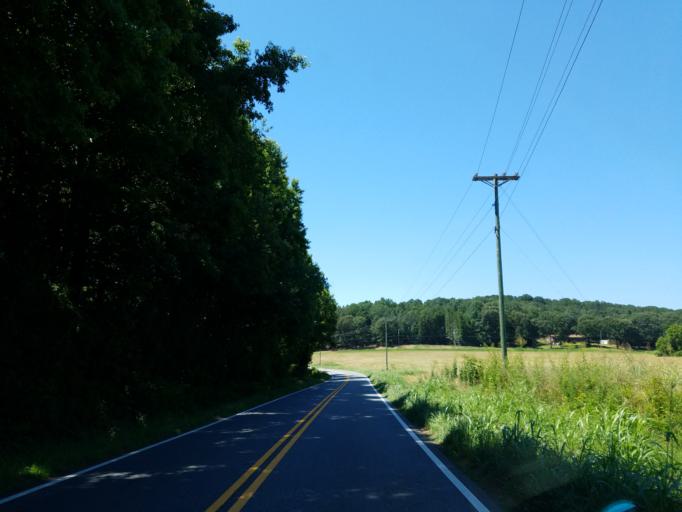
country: US
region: Georgia
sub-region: Forsyth County
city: Cumming
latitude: 34.2655
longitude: -84.0735
